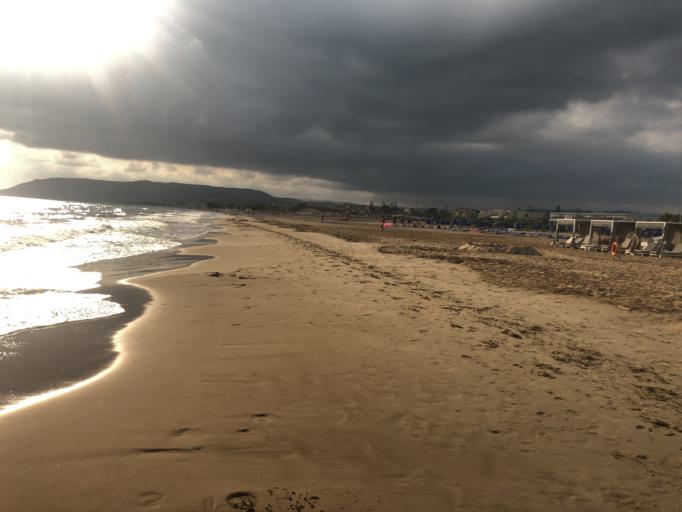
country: GR
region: Crete
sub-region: Nomos Chanias
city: Georgioupolis
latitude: 35.3549
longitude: 24.2908
